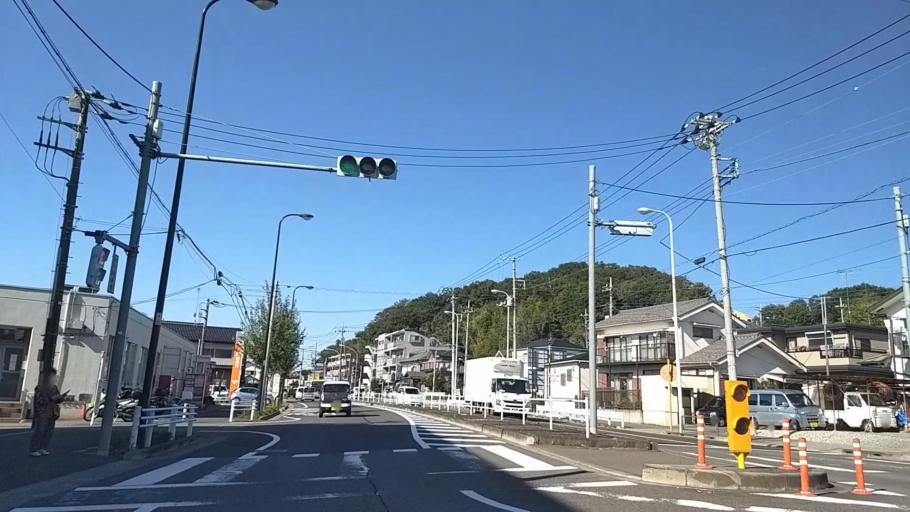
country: JP
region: Tokyo
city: Hachioji
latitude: 35.6001
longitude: 139.3611
